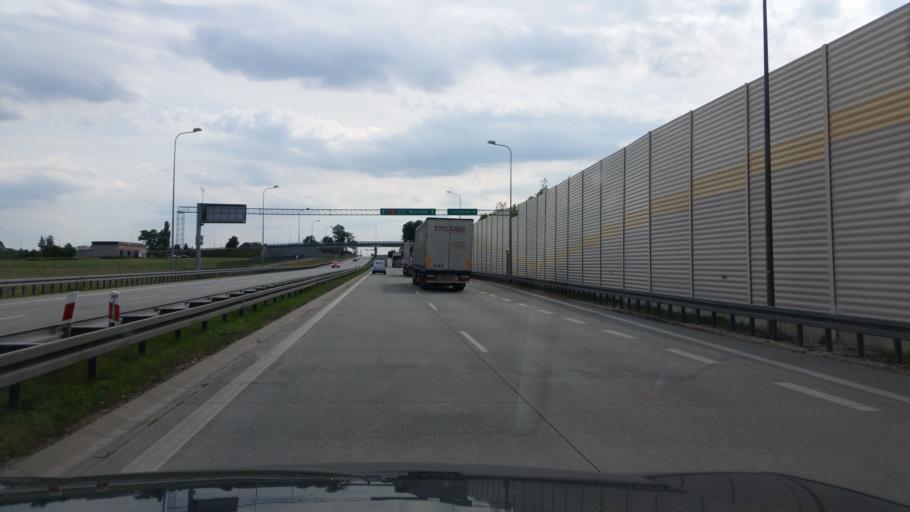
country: PL
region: Lodz Voivodeship
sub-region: Powiat rawski
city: Rawa Mazowiecka
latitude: 51.8065
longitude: 20.3036
